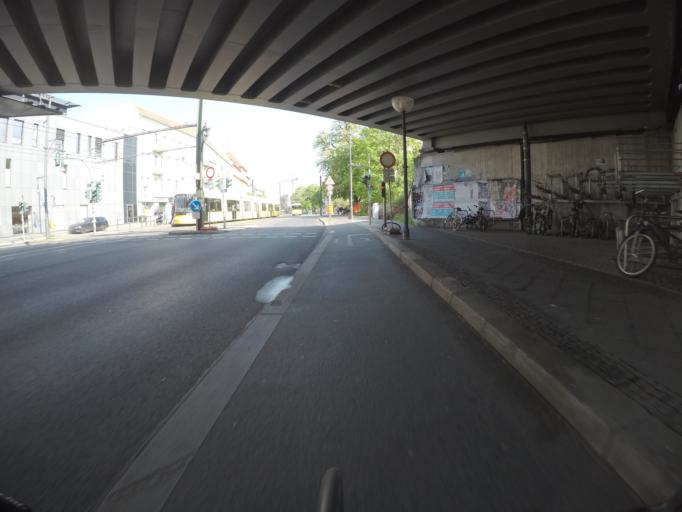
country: DE
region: Berlin
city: Pankow
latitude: 52.5674
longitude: 13.4124
